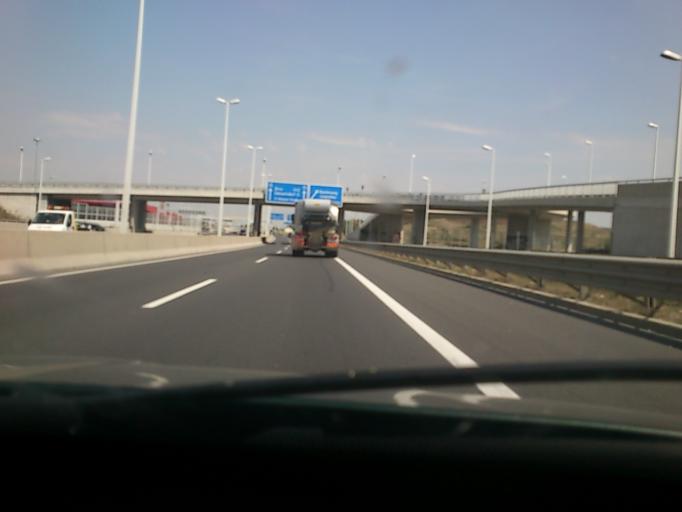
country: AT
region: Lower Austria
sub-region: Politischer Bezirk Wien-Umgebung
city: Gerasdorf bei Wien
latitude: 48.2545
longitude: 16.4738
